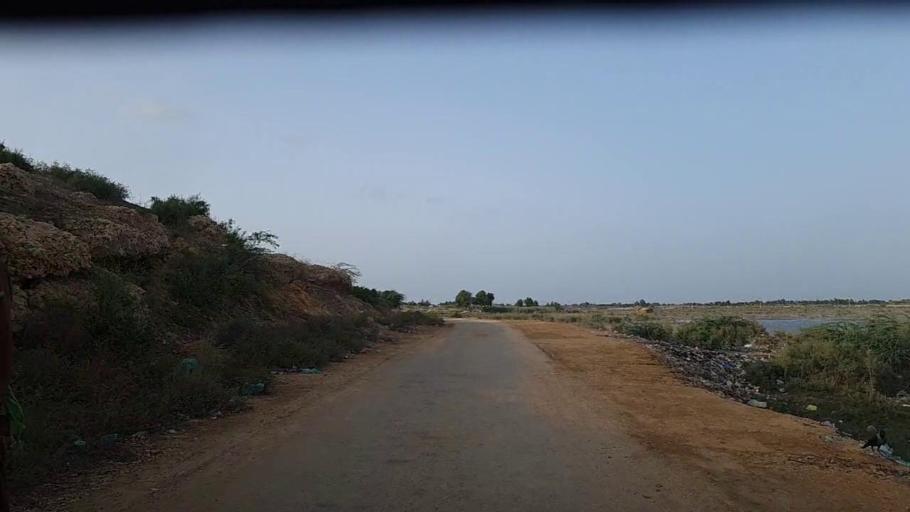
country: PK
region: Sindh
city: Thatta
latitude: 24.7539
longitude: 67.9016
